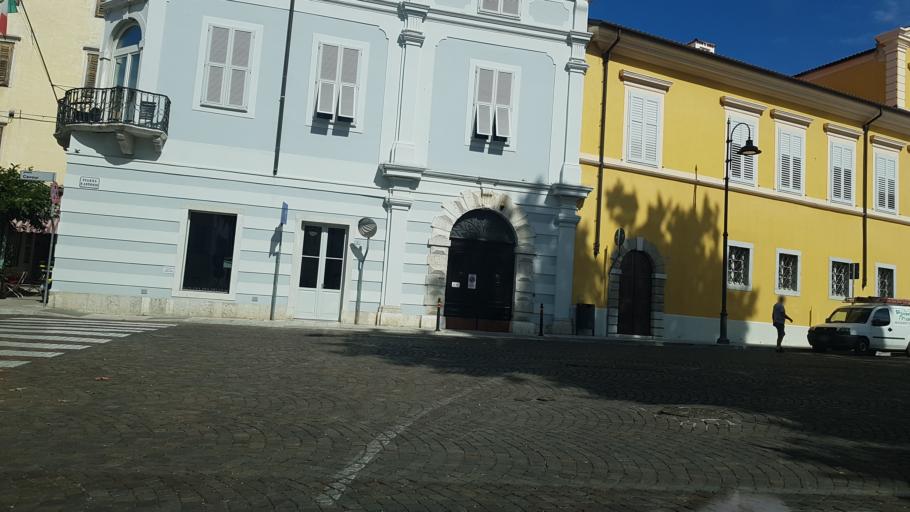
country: IT
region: Friuli Venezia Giulia
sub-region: Provincia di Gorizia
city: Gorizia
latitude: 45.9418
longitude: 13.6254
